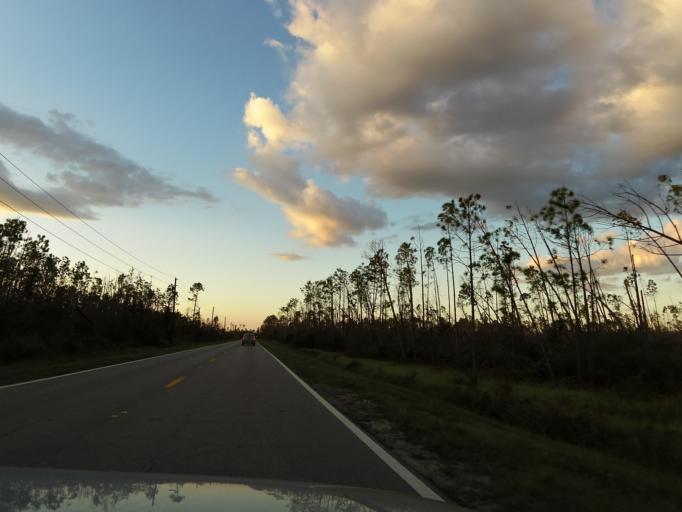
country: US
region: Florida
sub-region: Bay County
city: Mexico Beach
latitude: 29.9359
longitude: -85.3886
